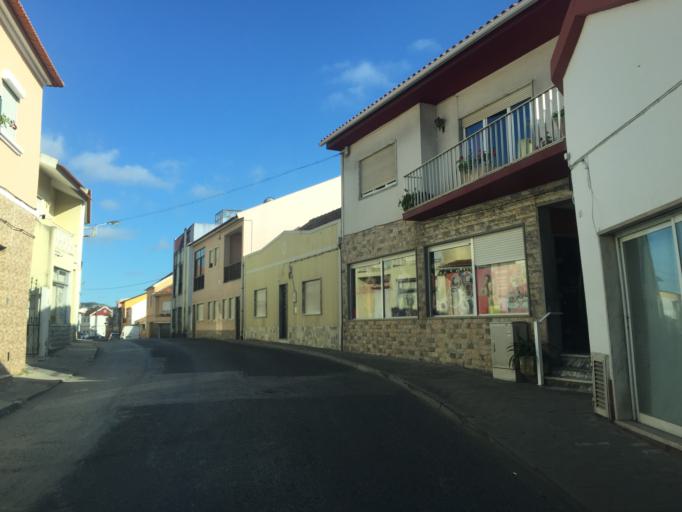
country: PT
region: Lisbon
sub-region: Torres Vedras
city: A dos Cunhados
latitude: 39.1508
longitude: -9.2979
